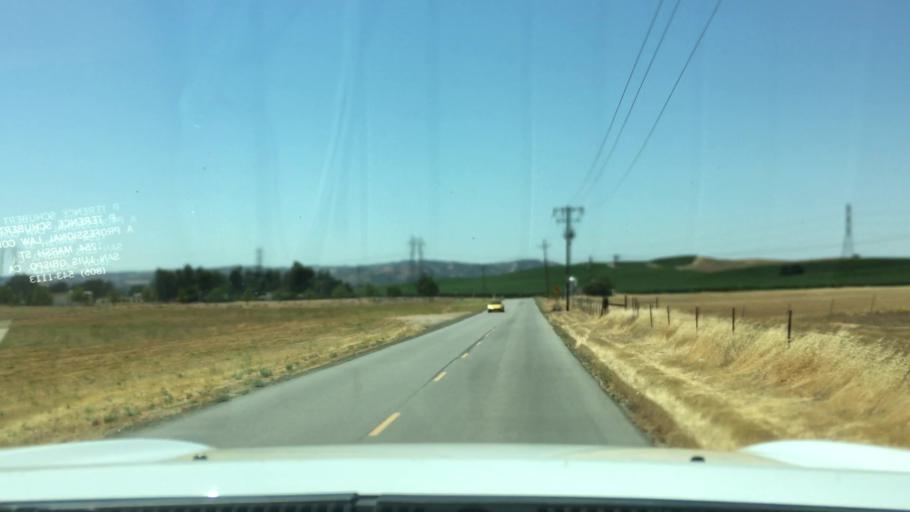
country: US
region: California
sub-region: San Luis Obispo County
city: Paso Robles
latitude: 35.6112
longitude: -120.6208
